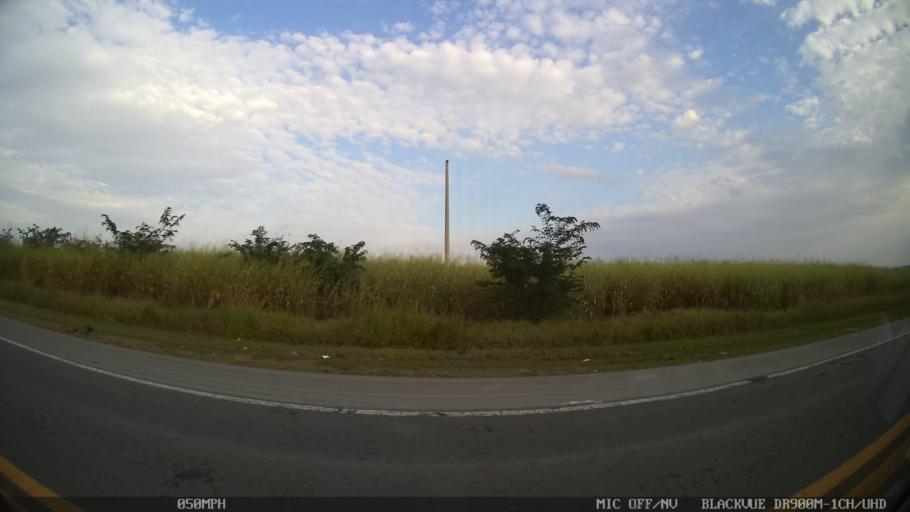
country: BR
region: Sao Paulo
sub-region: Americana
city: Americana
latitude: -22.6369
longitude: -47.3204
